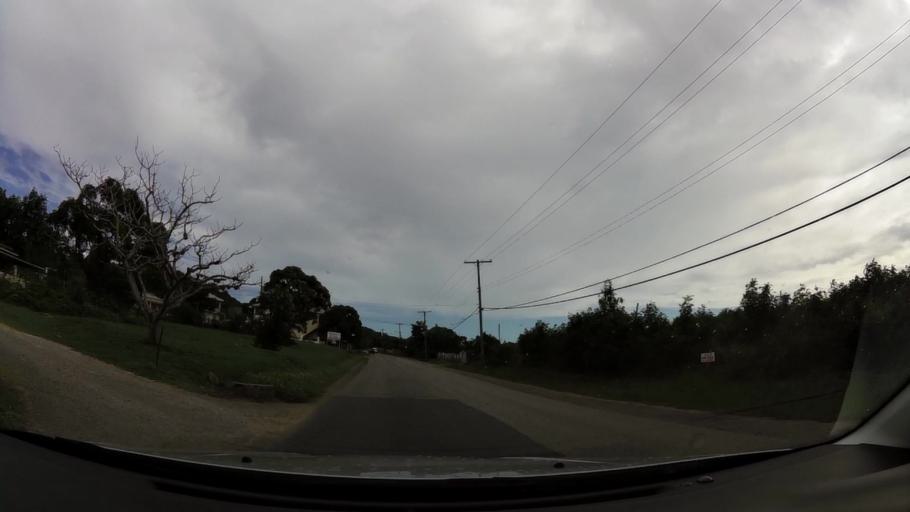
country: AG
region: Saint John
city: Potters Village
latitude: 17.0885
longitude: -61.8130
